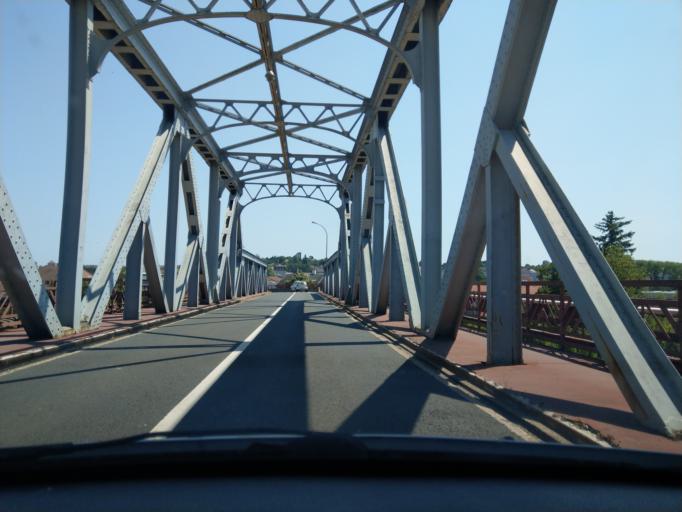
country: FR
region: Lorraine
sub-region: Departement de la Moselle
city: Sarrebourg
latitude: 48.7345
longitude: 7.0435
